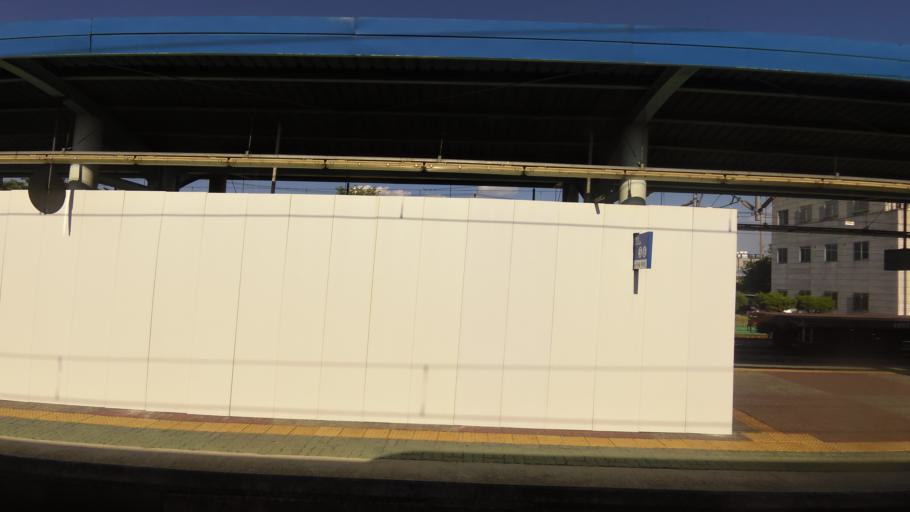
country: KR
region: Gyeongsangbuk-do
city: Waegwan
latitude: 35.9918
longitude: 128.4005
